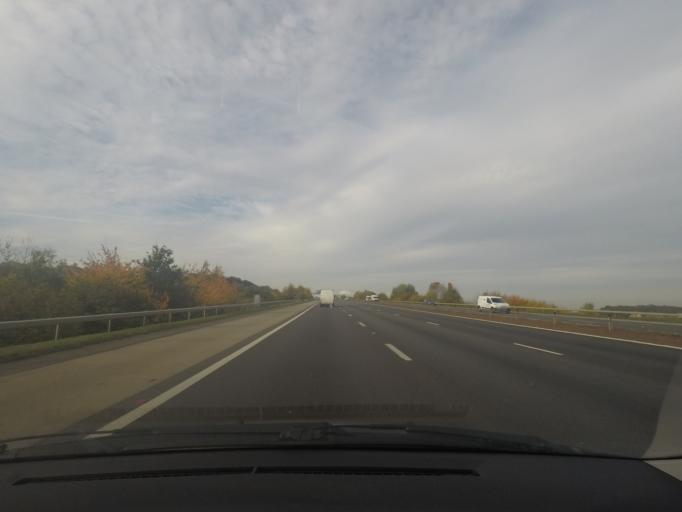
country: GB
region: England
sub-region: City and Borough of Leeds
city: Garforth
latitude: 53.8017
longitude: -1.4012
